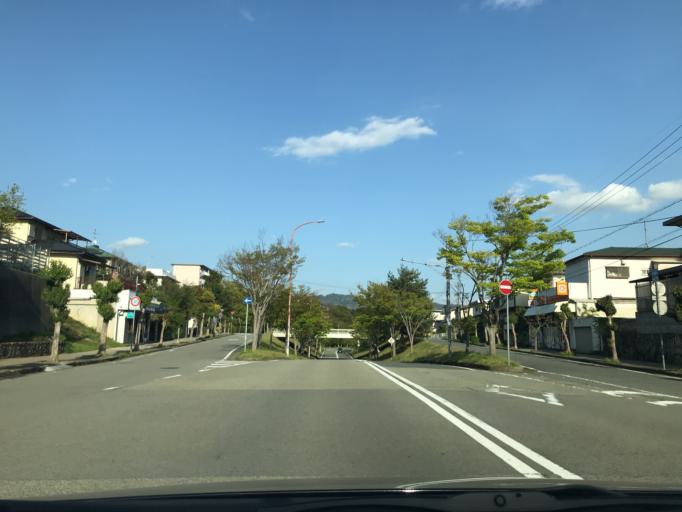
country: JP
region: Hyogo
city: Kawanishi
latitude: 34.8714
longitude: 135.3898
